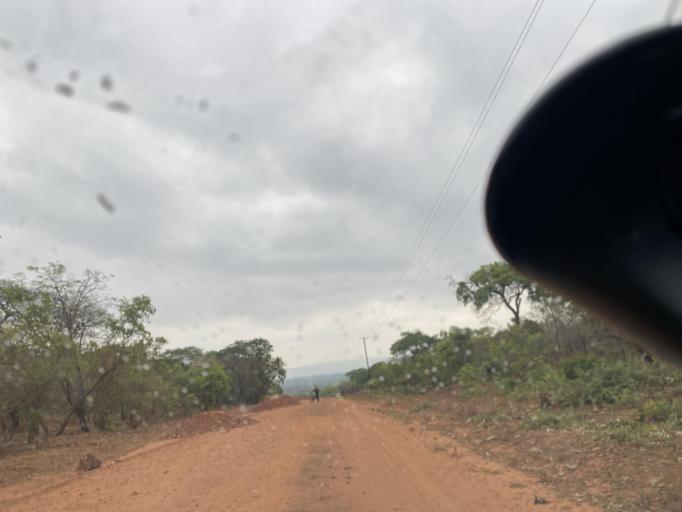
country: ZM
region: Lusaka
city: Chongwe
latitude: -15.1736
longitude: 28.7639
